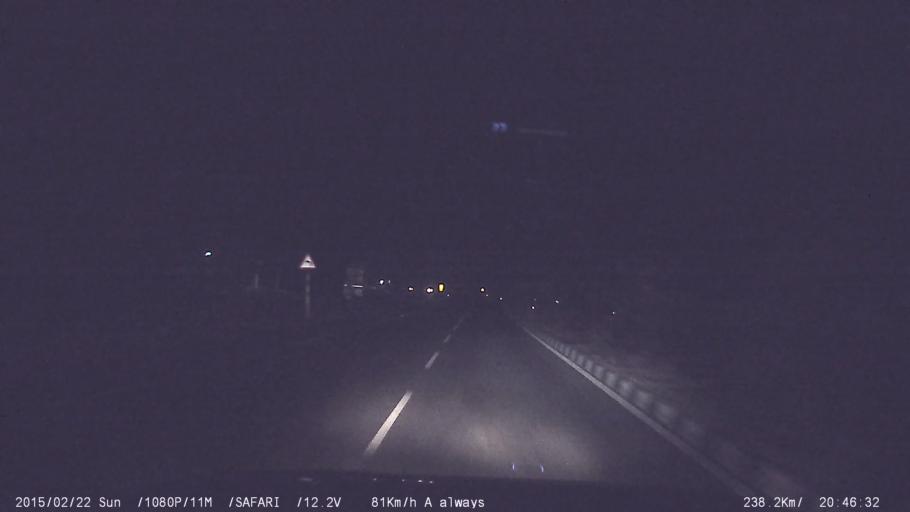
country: IN
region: Tamil Nadu
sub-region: Dindigul
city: Vedasandur
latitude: 10.4833
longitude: 77.9477
